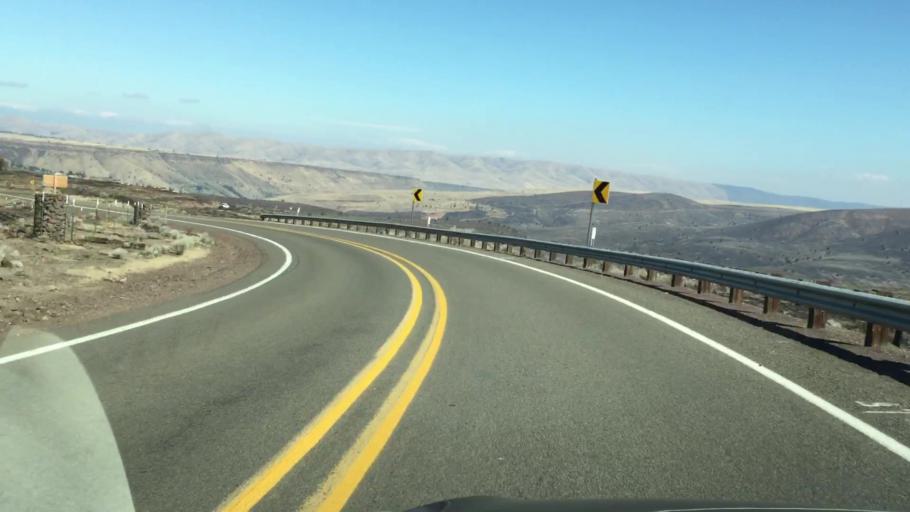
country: US
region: Oregon
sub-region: Jefferson County
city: Warm Springs
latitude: 45.1423
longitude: -121.0512
